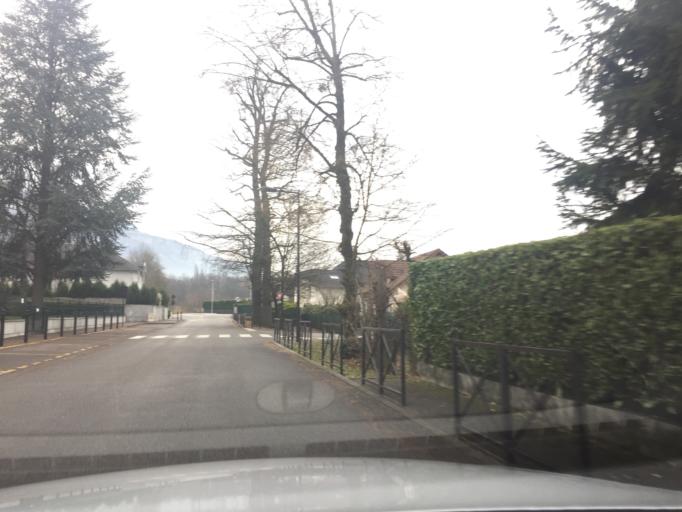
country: FR
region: Rhone-Alpes
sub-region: Departement de la Savoie
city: Drumettaz-Clarafond
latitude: 45.6599
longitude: 5.9159
